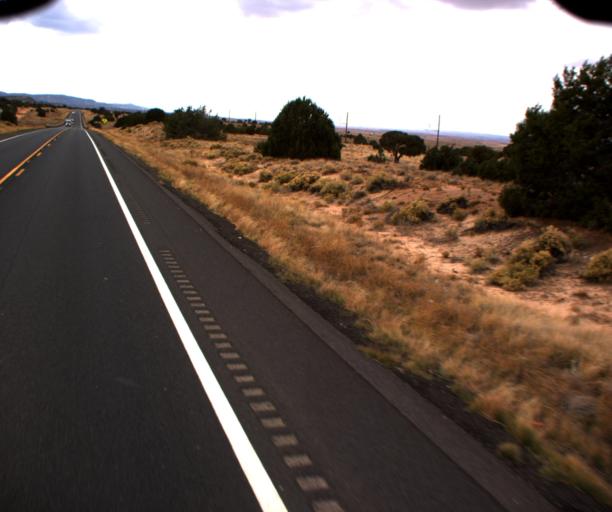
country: US
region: Arizona
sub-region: Navajo County
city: Kayenta
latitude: 36.4970
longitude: -110.6232
